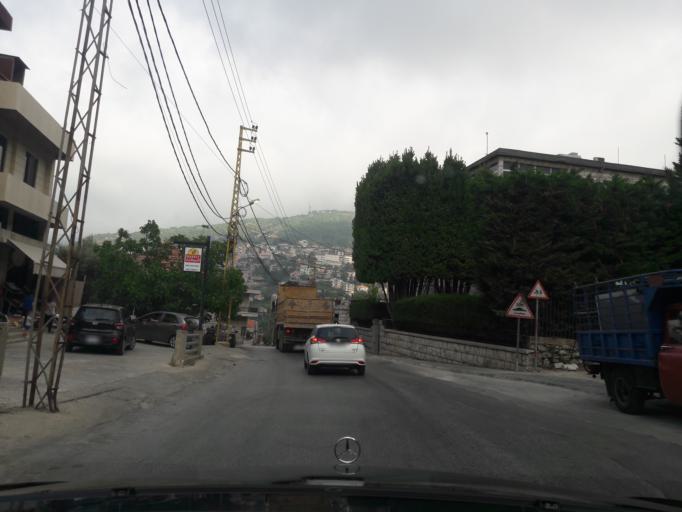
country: LB
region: Mont-Liban
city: Djounie
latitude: 33.9297
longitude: 35.7291
